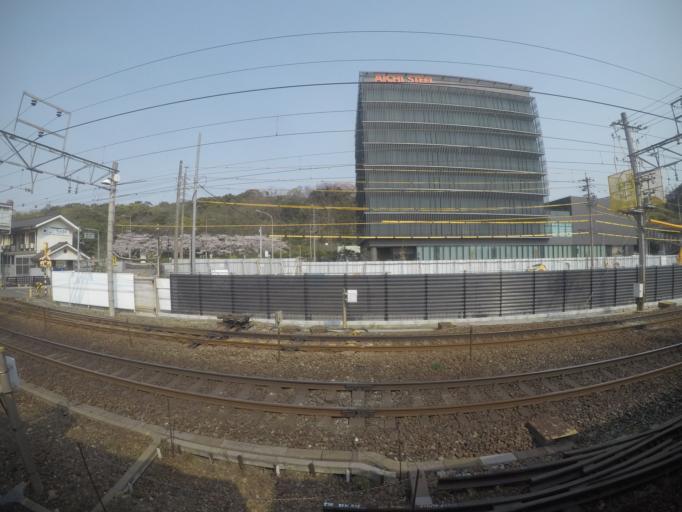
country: JP
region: Aichi
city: Obu
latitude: 35.0418
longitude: 136.9029
